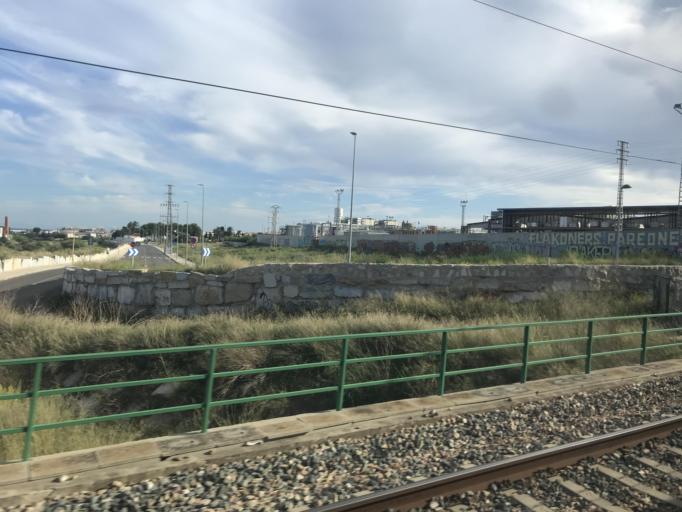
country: ES
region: Valencia
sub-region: Provincia de Castello
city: Benicarlo
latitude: 40.4310
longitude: 0.4180
